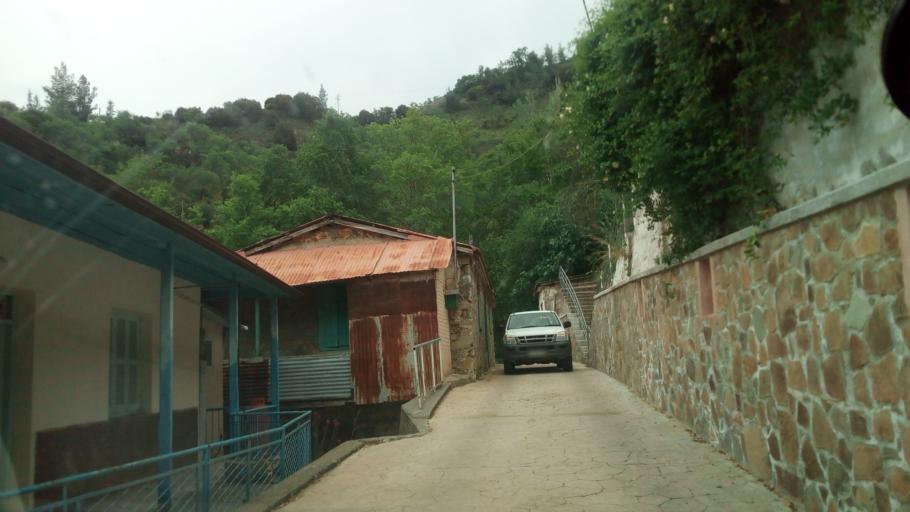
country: CY
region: Lefkosia
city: Kakopetria
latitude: 34.9614
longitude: 32.7510
